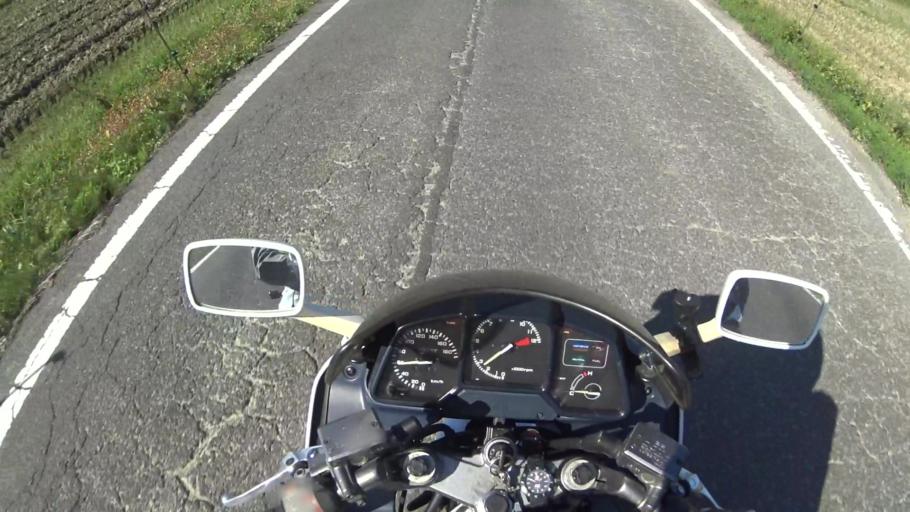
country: JP
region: Hyogo
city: Toyooka
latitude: 35.6364
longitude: 134.9455
